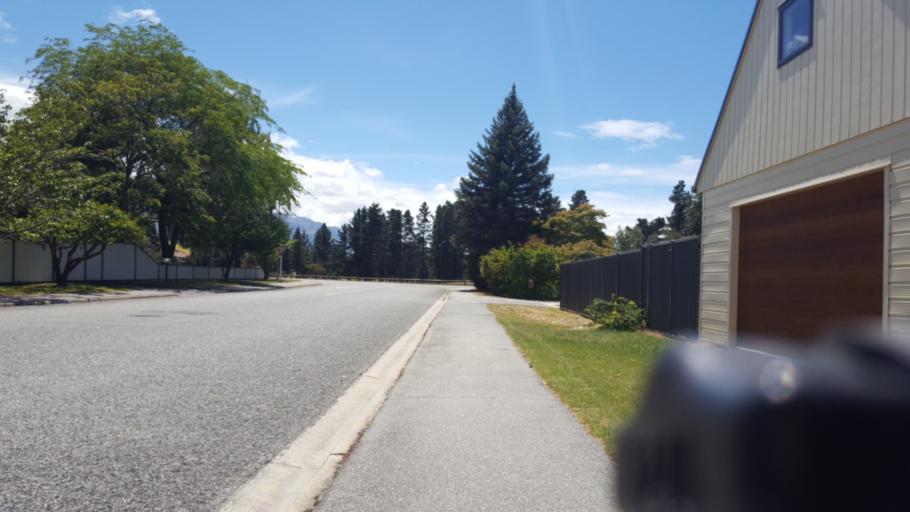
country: NZ
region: Otago
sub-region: Queenstown-Lakes District
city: Wanaka
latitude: -45.0407
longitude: 169.2020
